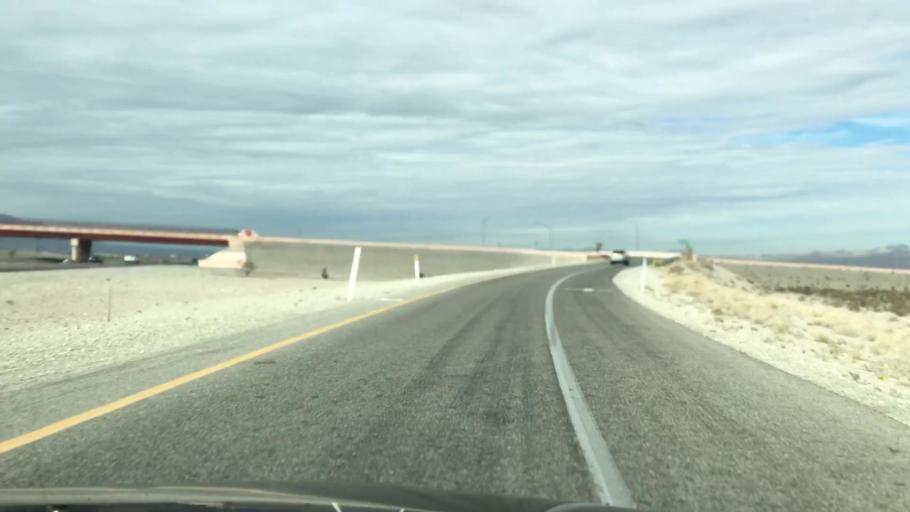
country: US
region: Nevada
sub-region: Clark County
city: Summerlin South
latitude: 36.3609
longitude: -115.3491
